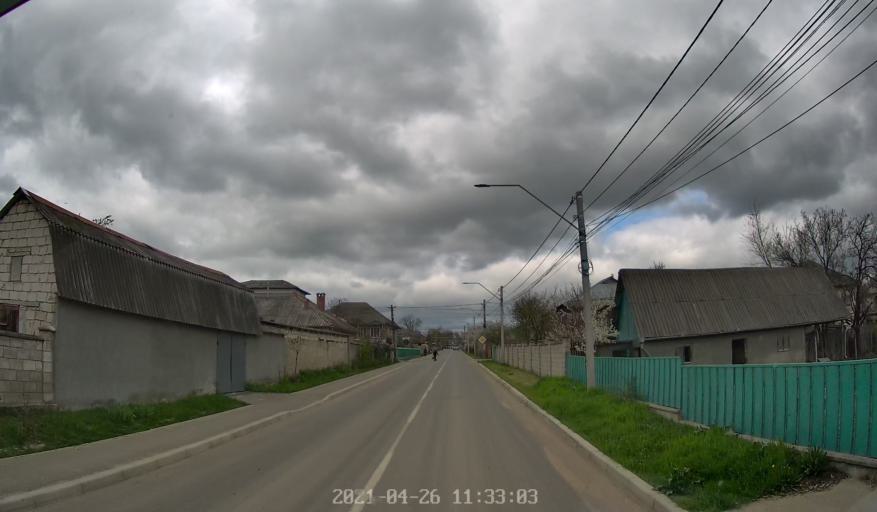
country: MD
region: Chisinau
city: Ciorescu
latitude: 47.1308
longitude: 28.8991
